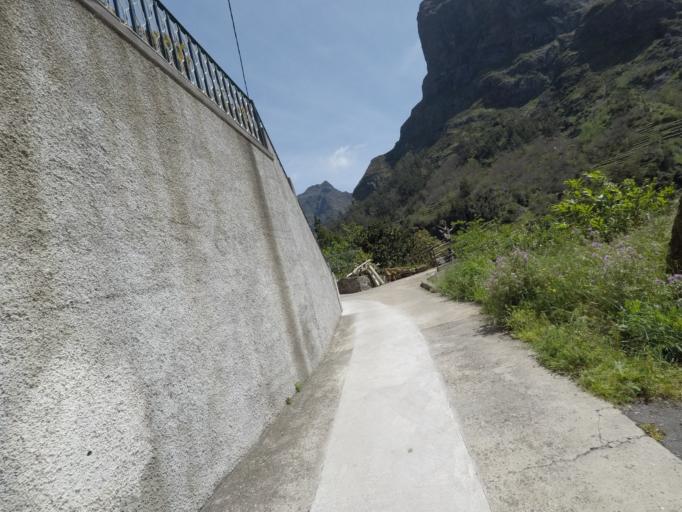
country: PT
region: Madeira
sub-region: Camara de Lobos
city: Curral das Freiras
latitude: 32.7310
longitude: -16.9702
